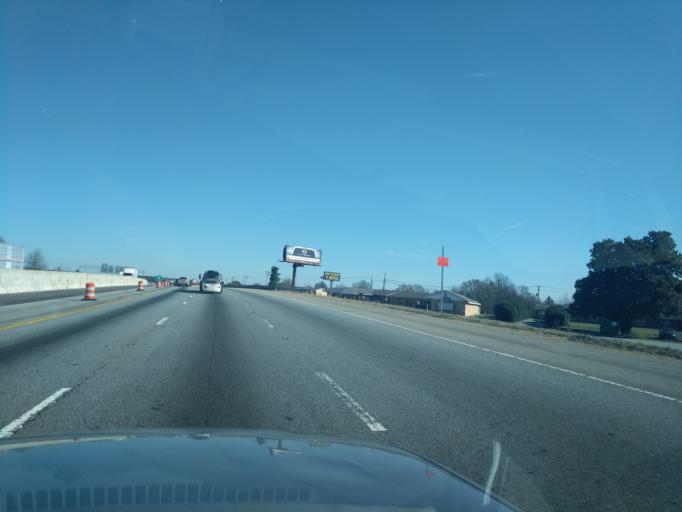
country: US
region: South Carolina
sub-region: Spartanburg County
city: Valley Falls
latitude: 35.0116
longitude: -81.9098
